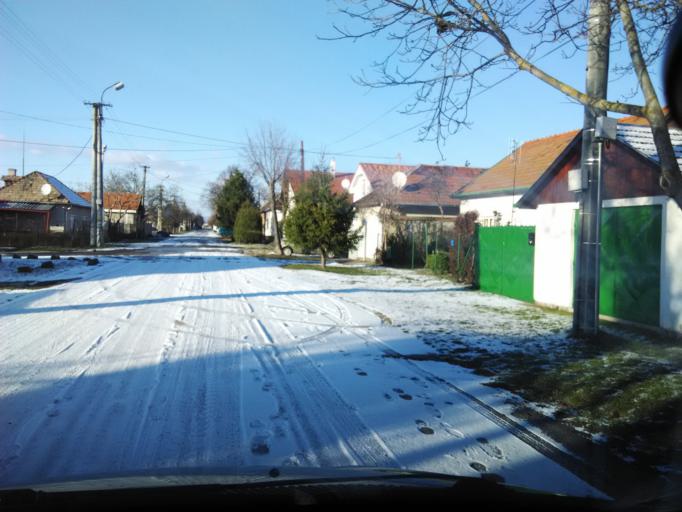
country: SK
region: Nitriansky
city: Levice
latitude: 48.2062
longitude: 18.5923
